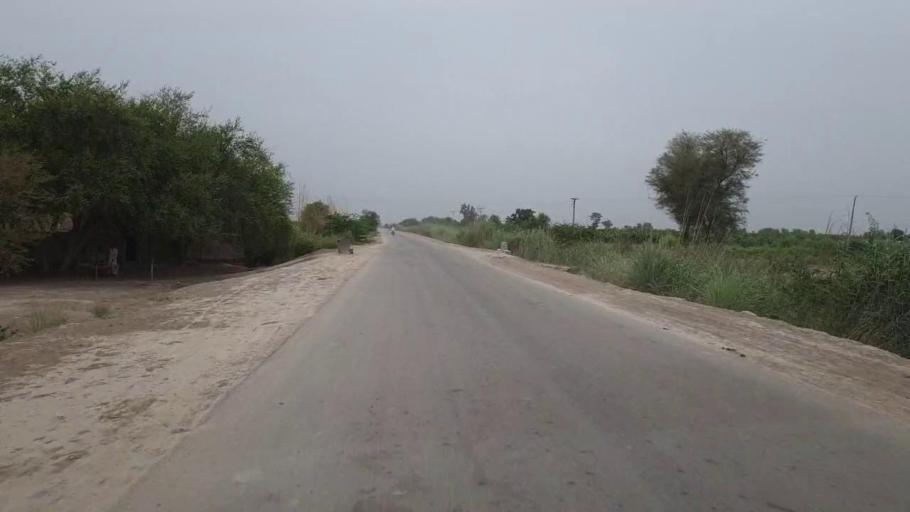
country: PK
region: Sindh
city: Bandhi
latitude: 26.5480
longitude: 68.2167
